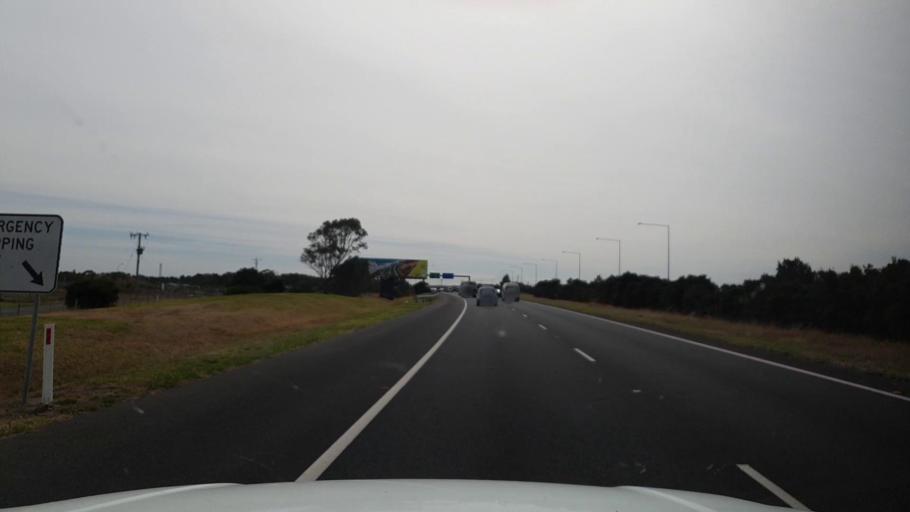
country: AU
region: Victoria
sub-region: Frankston
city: Carrum Downs
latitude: -38.0776
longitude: 145.1798
